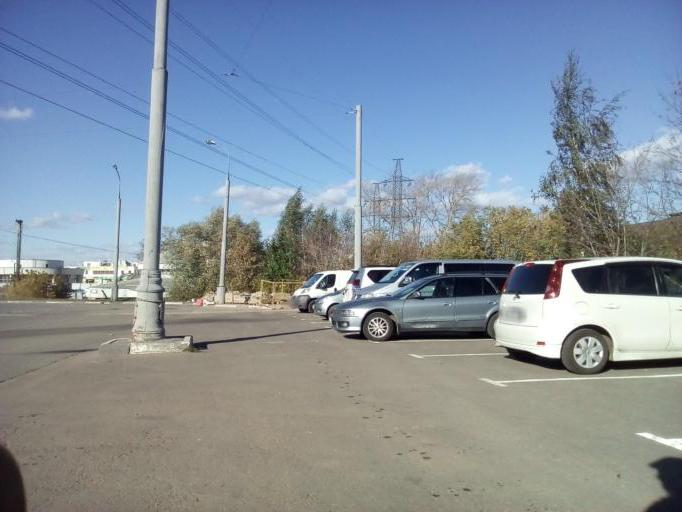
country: RU
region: Moscow
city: Novovladykino
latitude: 55.8463
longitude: 37.5916
